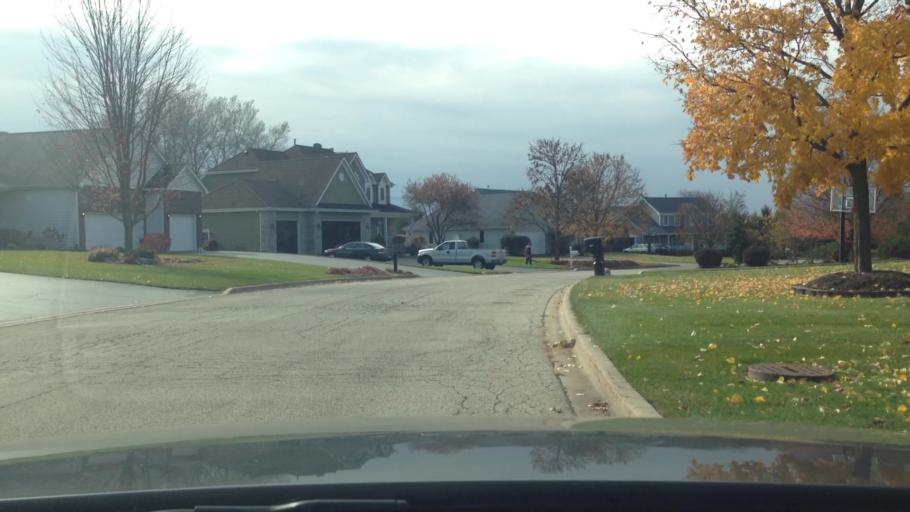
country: US
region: Illinois
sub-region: McHenry County
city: Woodstock
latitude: 42.2994
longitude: -88.4781
